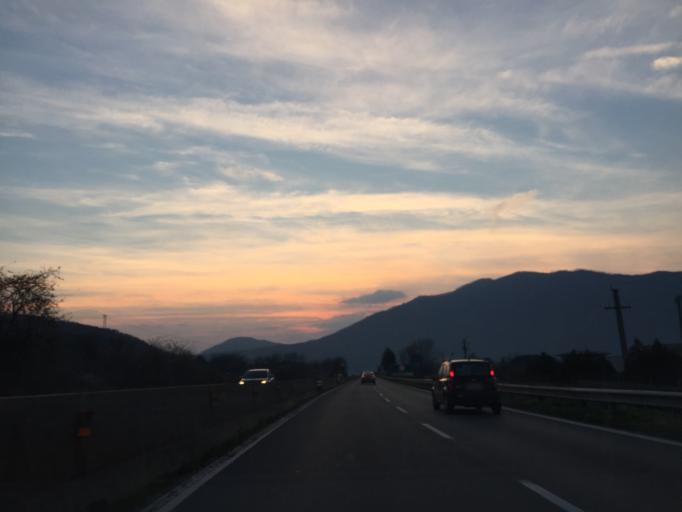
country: IT
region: Campania
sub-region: Provincia di Avellino
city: Montoro Superiore
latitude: 40.8177
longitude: 14.7930
